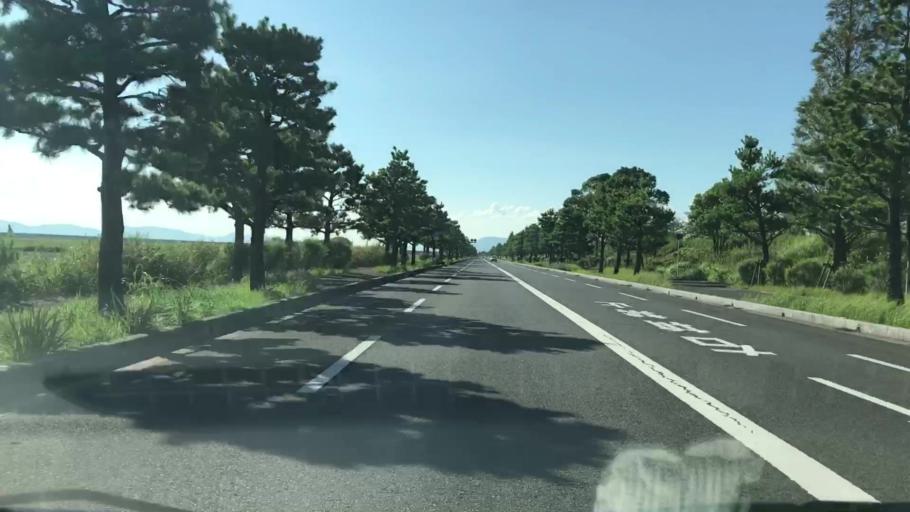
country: JP
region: Saga Prefecture
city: Okawa
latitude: 33.1554
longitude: 130.3015
